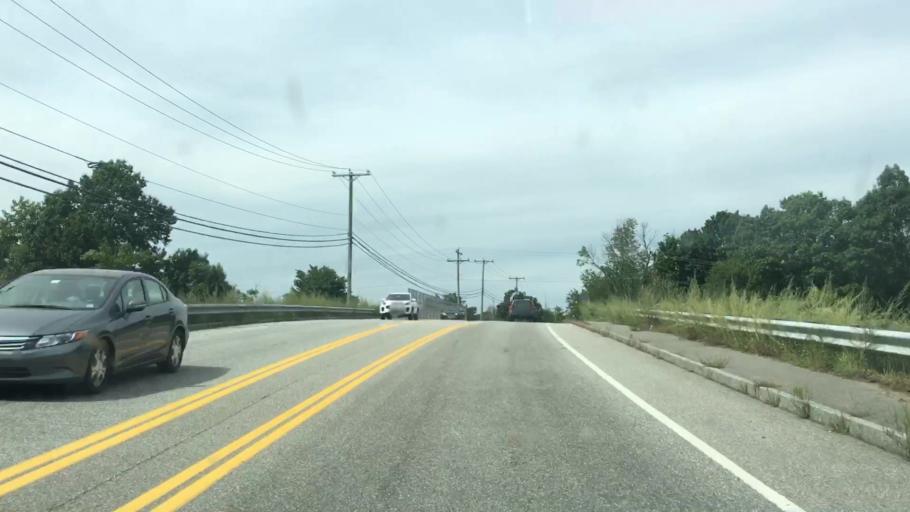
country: US
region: New Hampshire
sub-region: Strafford County
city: Dover
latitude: 43.1864
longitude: -70.8969
